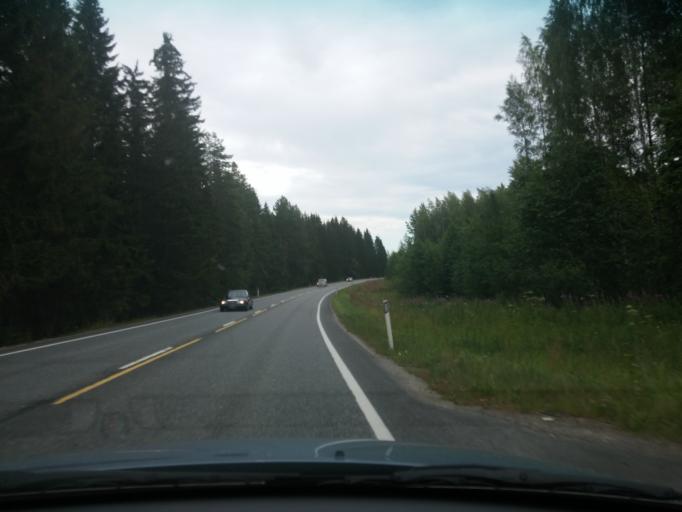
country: FI
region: Haeme
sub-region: Haemeenlinna
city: Tervakoski
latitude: 60.7451
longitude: 24.6614
